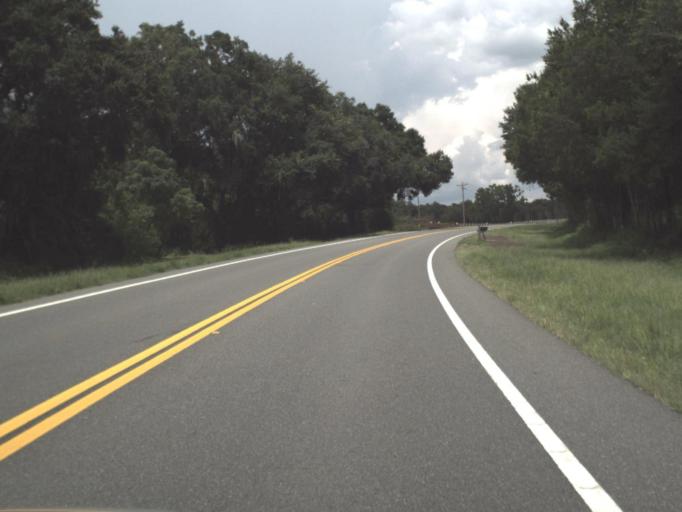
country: US
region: Florida
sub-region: Alachua County
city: Alachua
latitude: 29.8108
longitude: -82.4698
